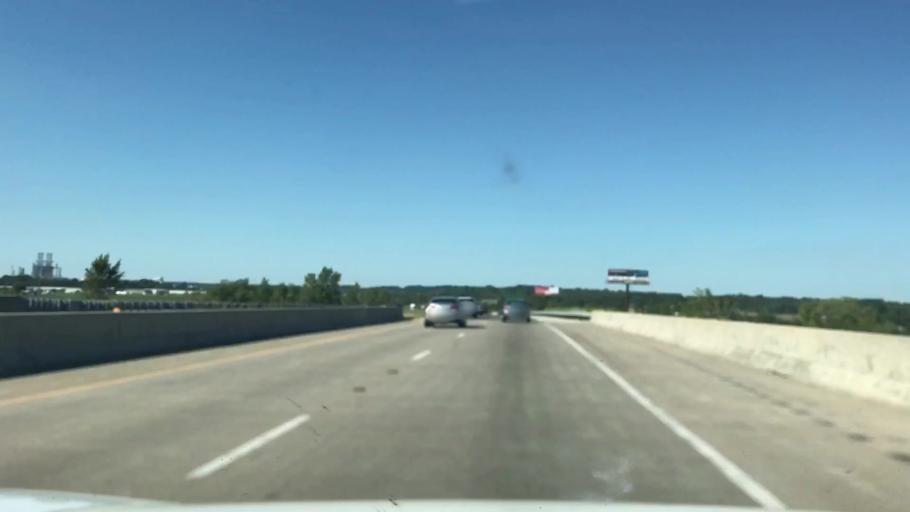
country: US
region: Illinois
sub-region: Madison County
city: South Roxana
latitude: 38.8175
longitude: -90.0420
